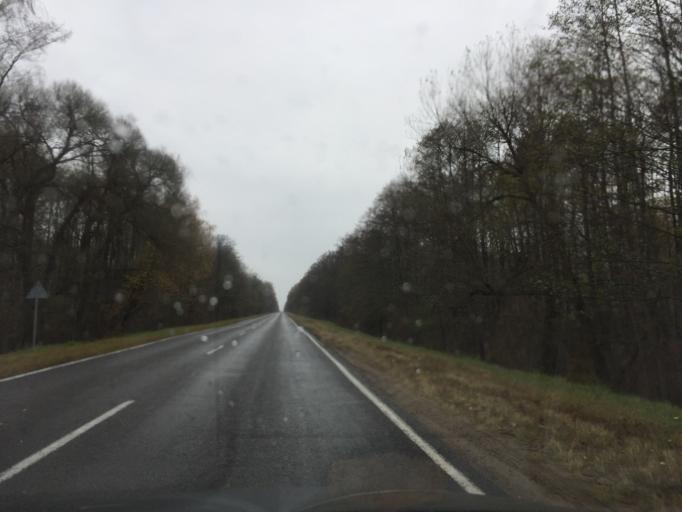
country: BY
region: Mogilev
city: Slawharad
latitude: 53.3748
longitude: 30.8703
